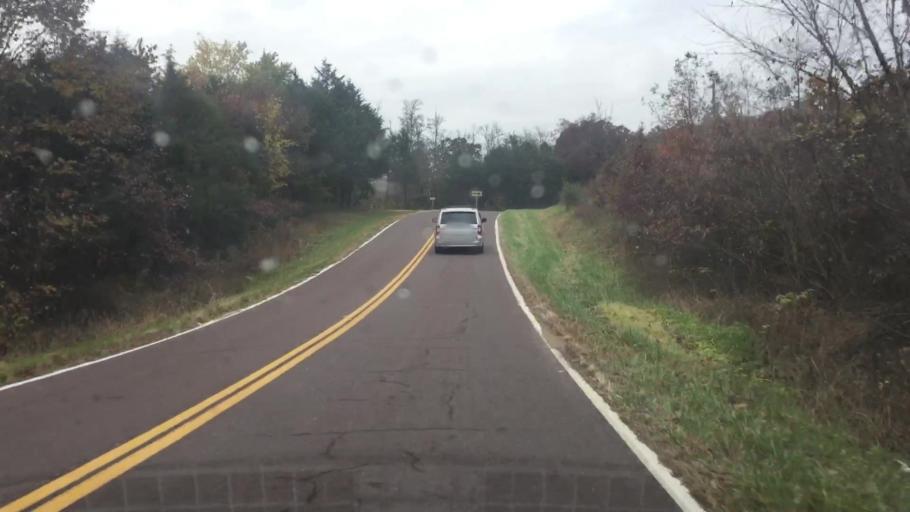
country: US
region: Missouri
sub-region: Callaway County
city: Fulton
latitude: 38.7877
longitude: -91.7606
